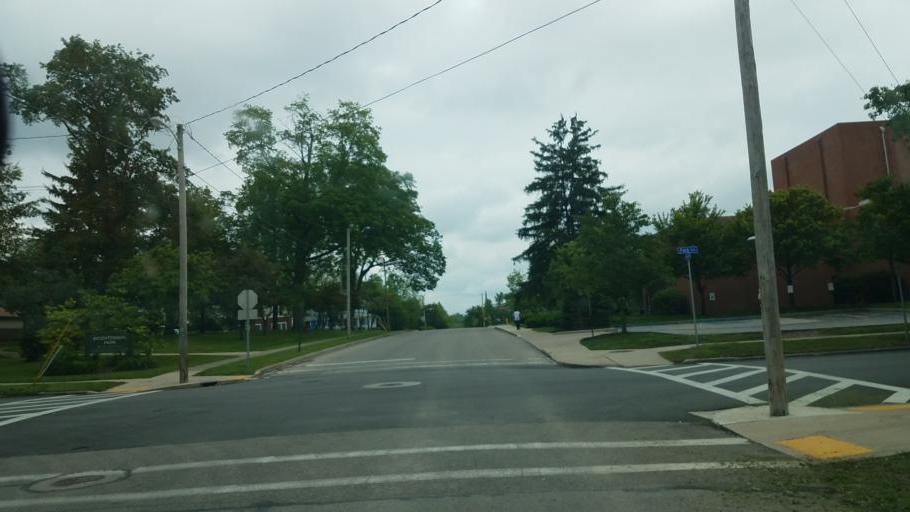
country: US
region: Ohio
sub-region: Delaware County
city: Delaware
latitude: 40.2953
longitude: -83.0715
